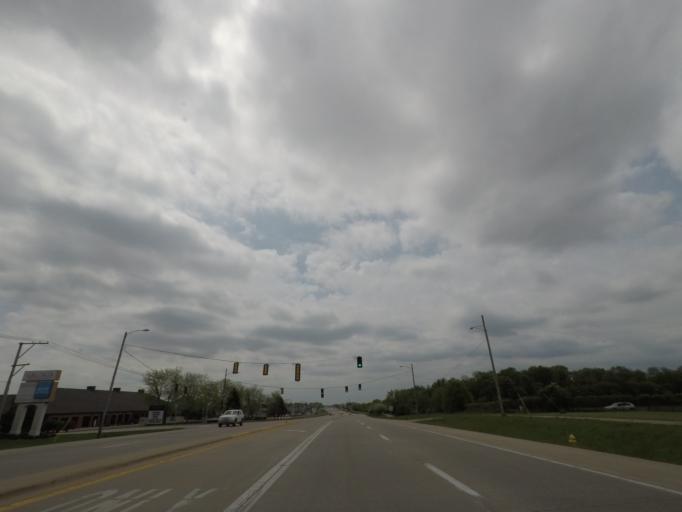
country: US
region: Illinois
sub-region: Winnebago County
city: Cherry Valley
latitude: 42.2782
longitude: -88.9798
